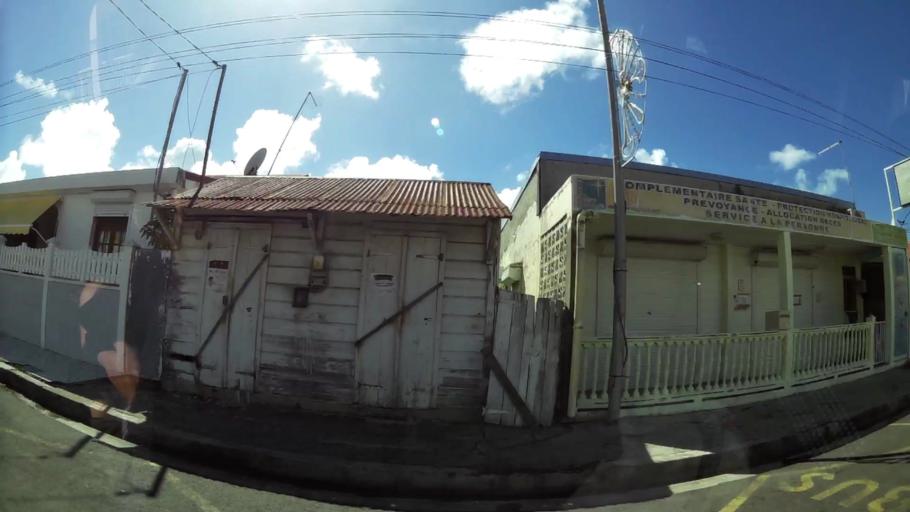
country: GP
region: Guadeloupe
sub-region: Guadeloupe
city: Le Moule
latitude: 16.3304
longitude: -61.3451
